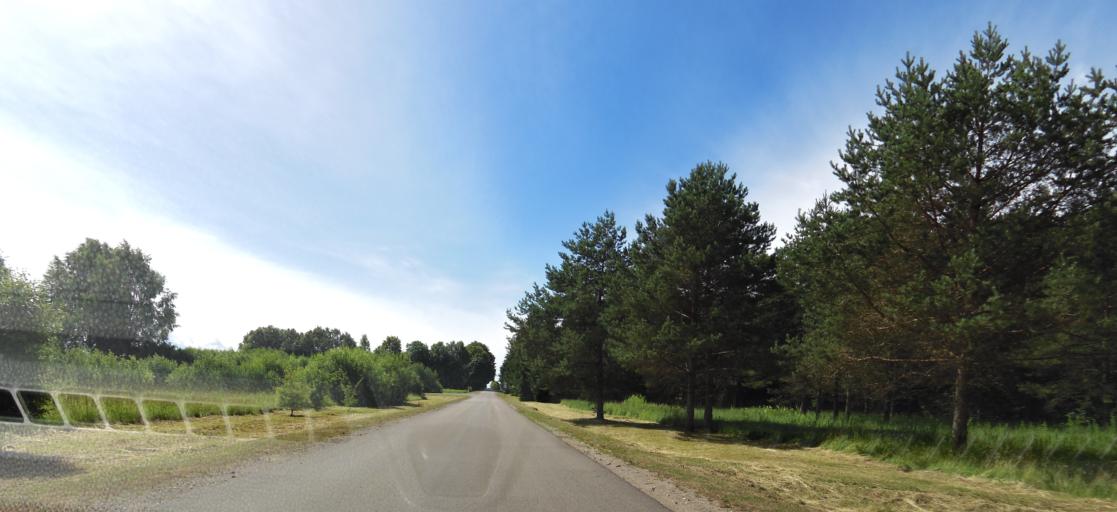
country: LT
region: Panevezys
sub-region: Birzai
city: Birzai
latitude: 56.1841
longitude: 24.7596
